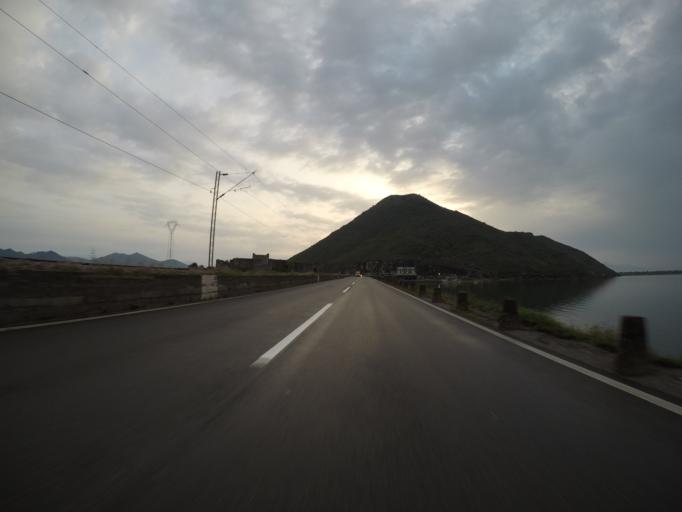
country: ME
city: Mojanovici
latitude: 42.2703
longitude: 19.1187
